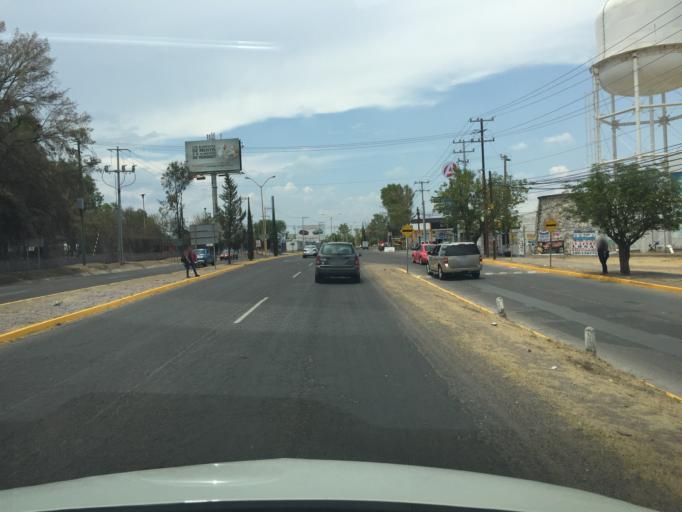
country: MX
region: Aguascalientes
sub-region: Aguascalientes
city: La Loma de los Negritos
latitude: 21.8599
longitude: -102.3398
